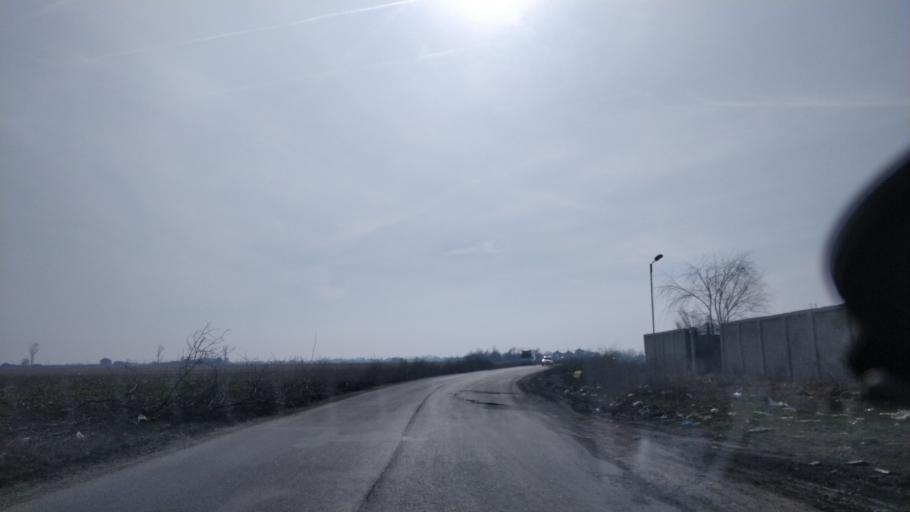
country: RO
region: Giurgiu
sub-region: Comuna Bolintin Vale
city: Bolintin Vale
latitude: 44.4570
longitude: 25.7813
